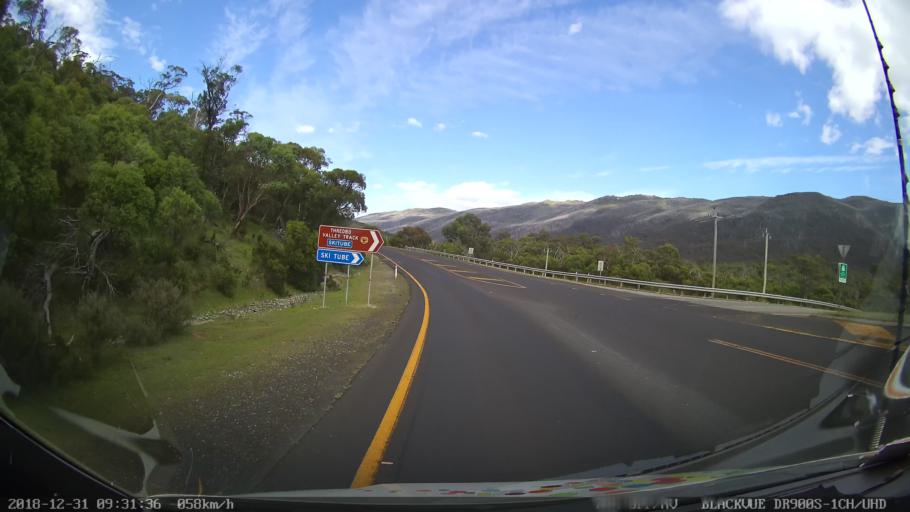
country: AU
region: New South Wales
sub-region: Snowy River
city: Jindabyne
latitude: -36.4491
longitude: 148.4424
